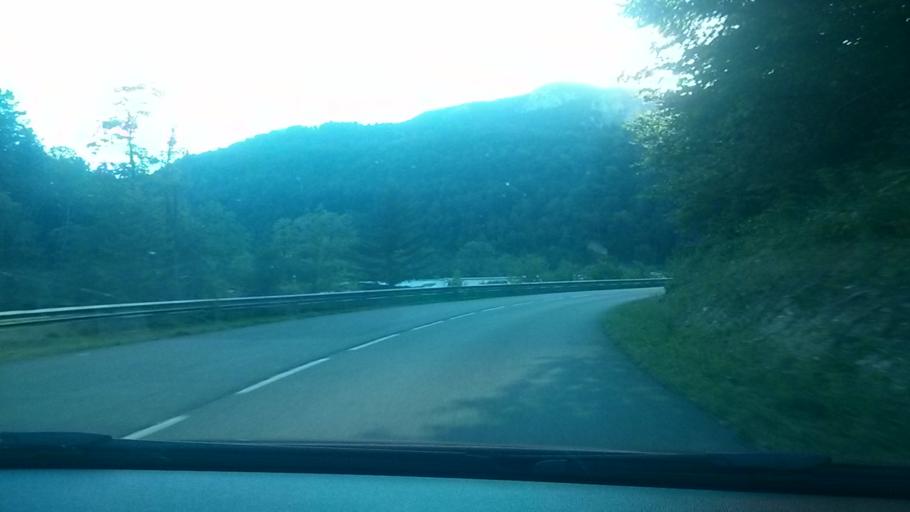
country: FR
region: Franche-Comte
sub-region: Departement du Jura
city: Saint-Claude
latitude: 46.3756
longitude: 5.8765
